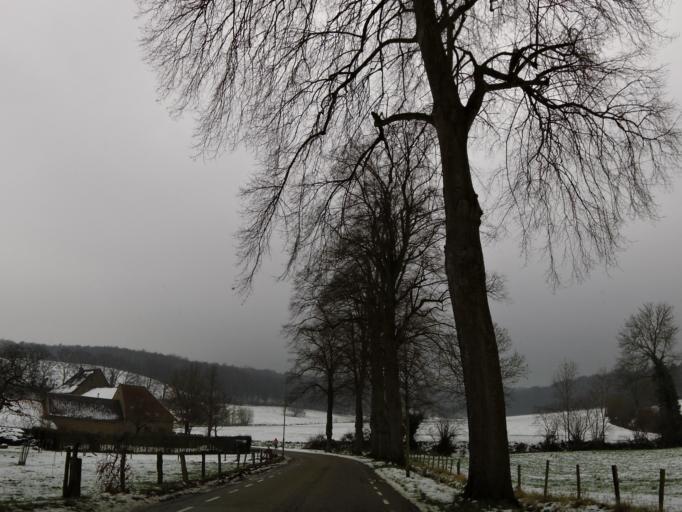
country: NL
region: Limburg
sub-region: Gemeente Vaals
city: Vaals
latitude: 50.7749
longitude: 5.9770
